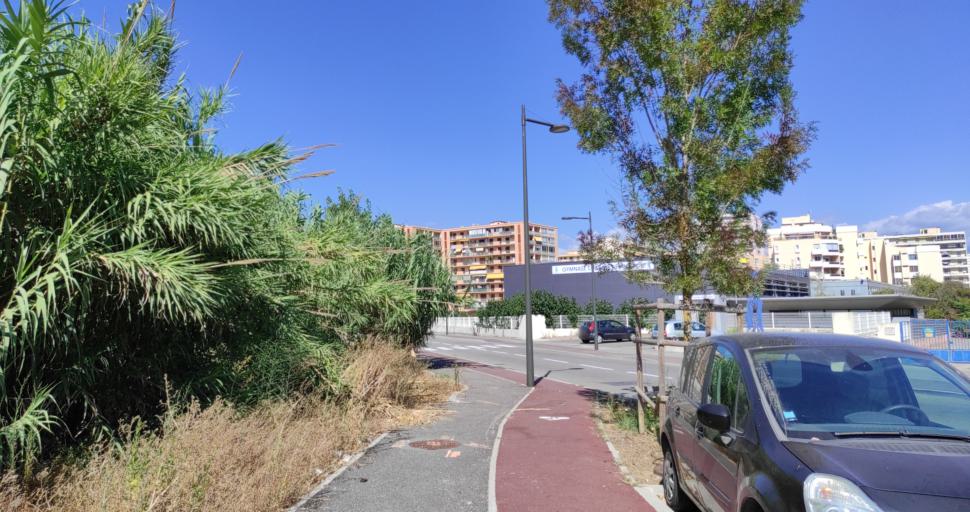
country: FR
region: Corsica
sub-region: Departement de la Corse-du-Sud
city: Ajaccio
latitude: 41.9356
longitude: 8.7371
